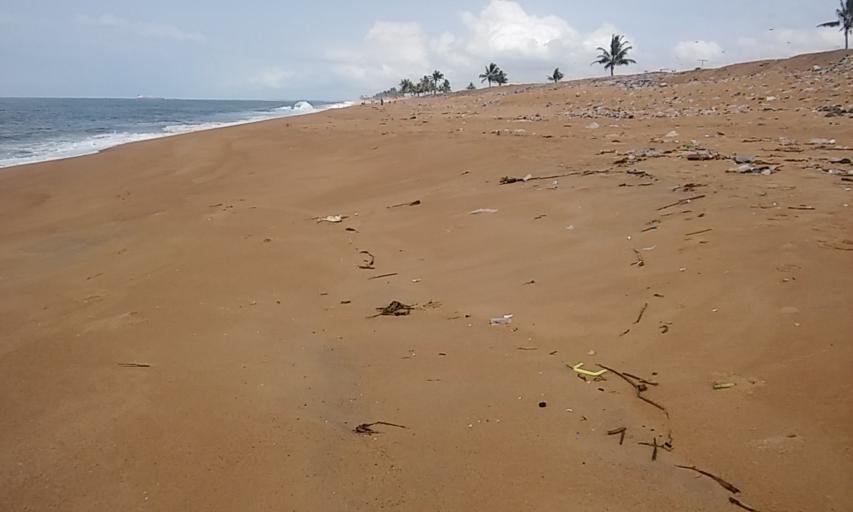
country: CI
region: Lagunes
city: Bingerville
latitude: 5.2386
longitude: -3.8980
